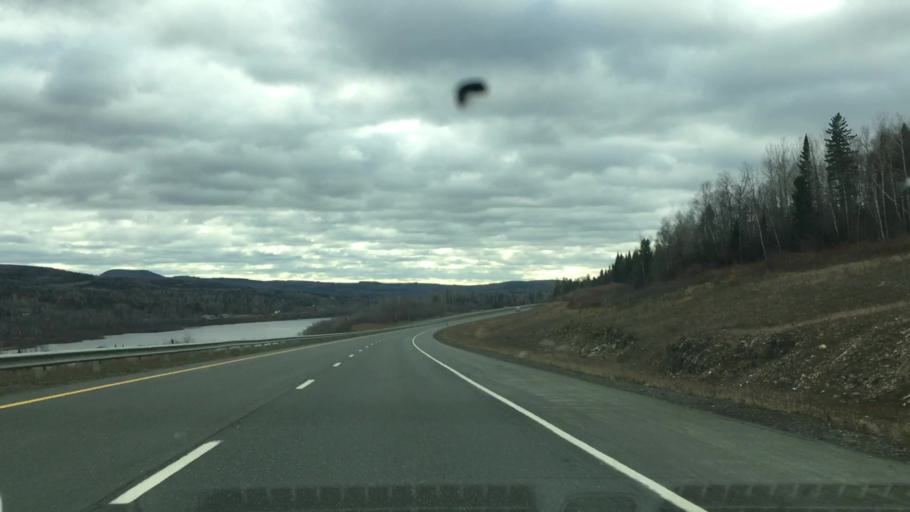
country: US
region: Maine
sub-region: Aroostook County
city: Fort Fairfield
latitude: 46.6822
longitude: -67.7327
